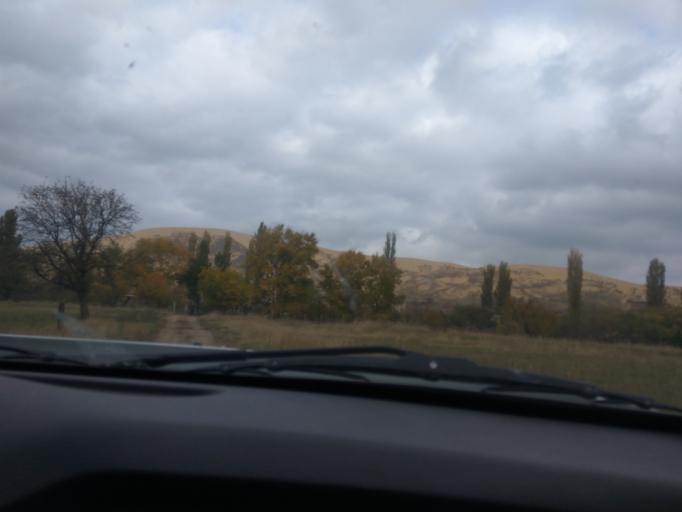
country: RU
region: Dagestan
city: Korkmaskala
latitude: 43.0014
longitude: 47.2402
